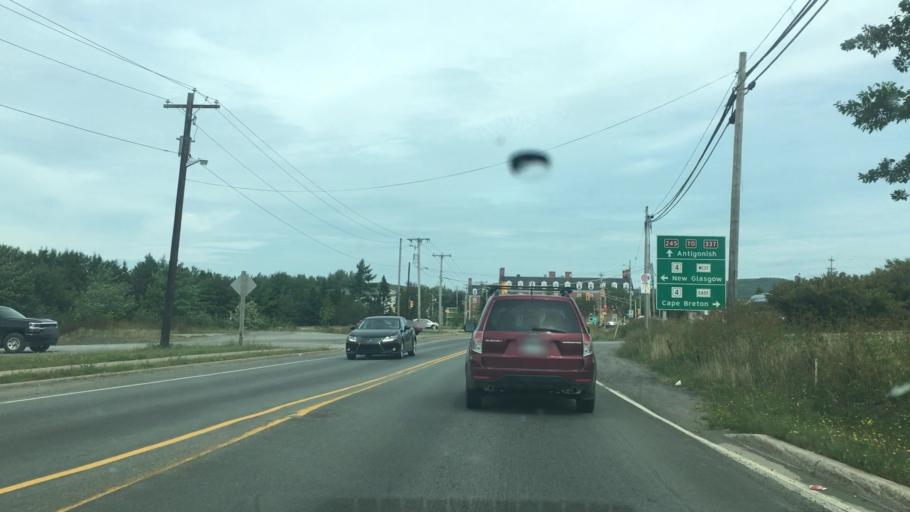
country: CA
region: Nova Scotia
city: Antigonish
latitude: 45.6129
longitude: -61.9988
